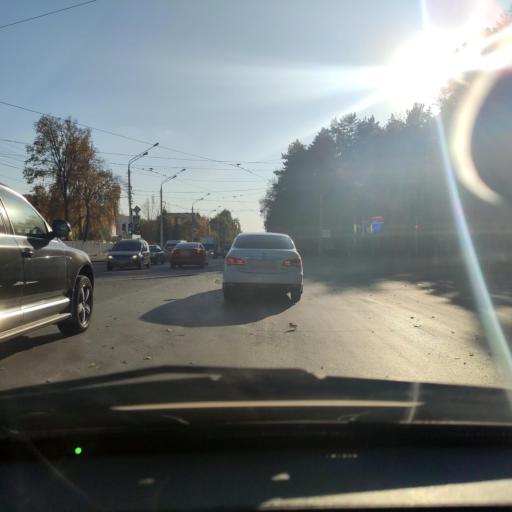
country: RU
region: Bashkortostan
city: Ufa
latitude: 54.7668
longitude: 56.0098
